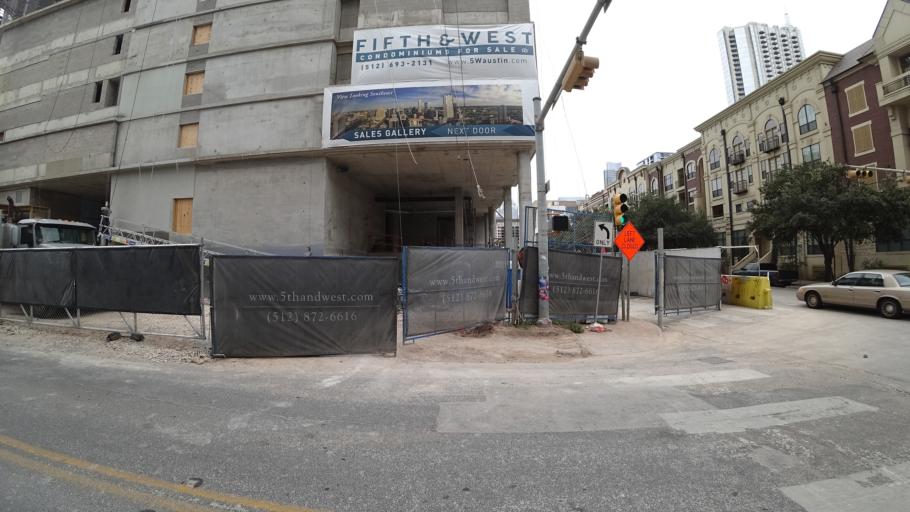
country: US
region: Texas
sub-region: Travis County
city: Austin
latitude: 30.2695
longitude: -97.7509
